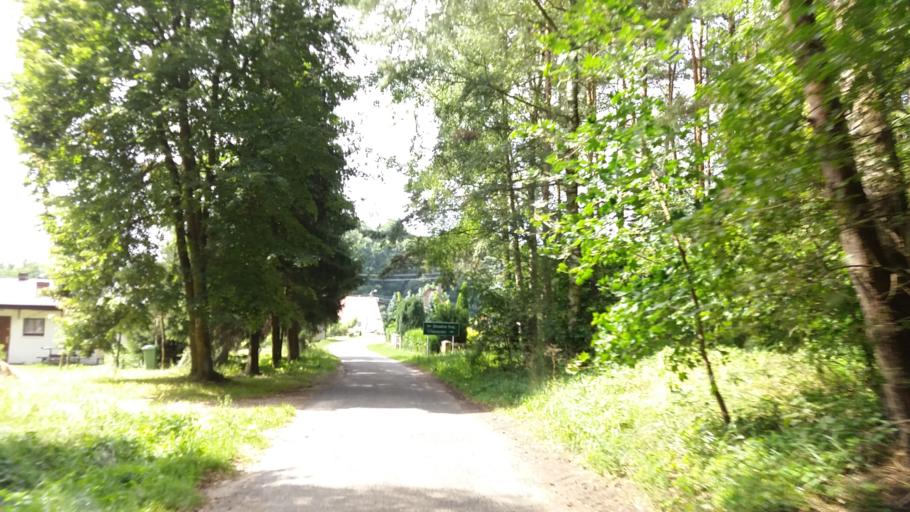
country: PL
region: West Pomeranian Voivodeship
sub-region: Powiat choszczenski
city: Krzecin
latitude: 53.0851
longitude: 15.4827
